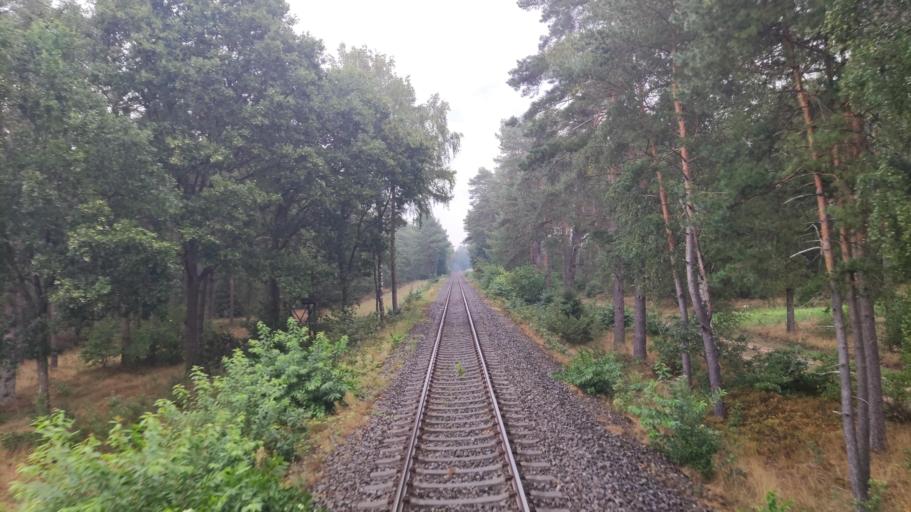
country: DE
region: Lower Saxony
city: Bispingen
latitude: 53.0464
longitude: 9.9434
